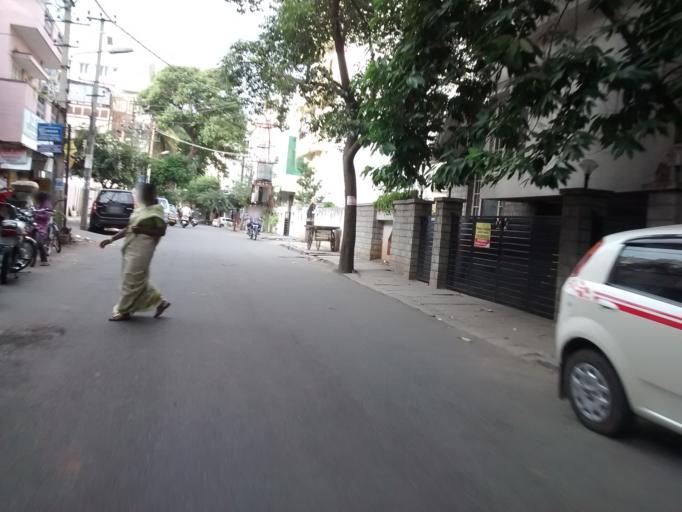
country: IN
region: Karnataka
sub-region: Bangalore Urban
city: Bangalore
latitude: 12.9347
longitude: 77.5632
